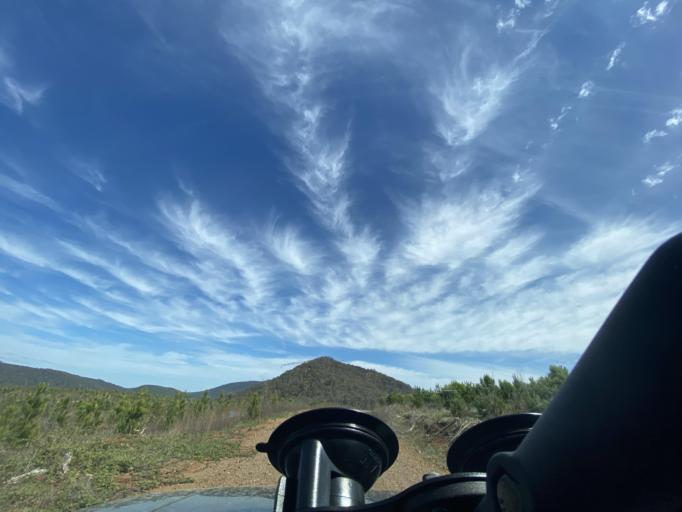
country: AU
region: Victoria
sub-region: Mansfield
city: Mansfield
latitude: -36.8279
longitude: 146.1030
